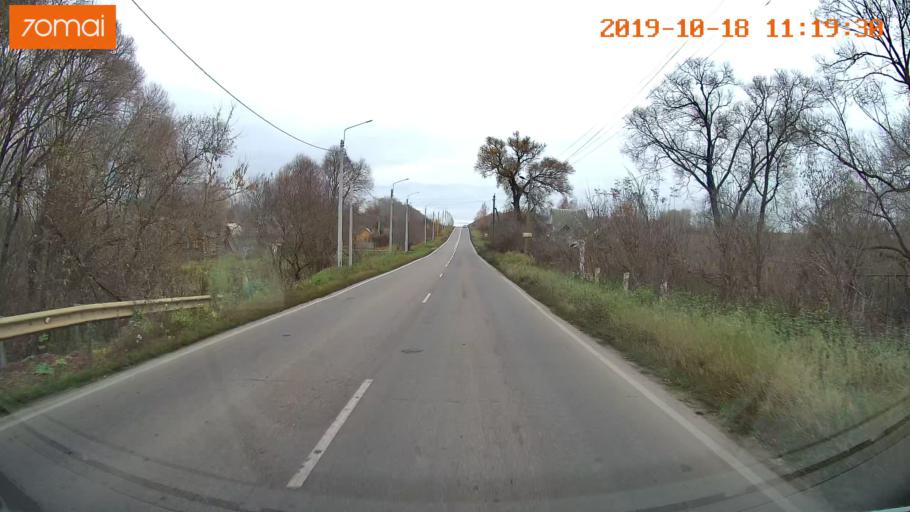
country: RU
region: Tula
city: Kimovsk
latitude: 54.0471
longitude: 38.5542
